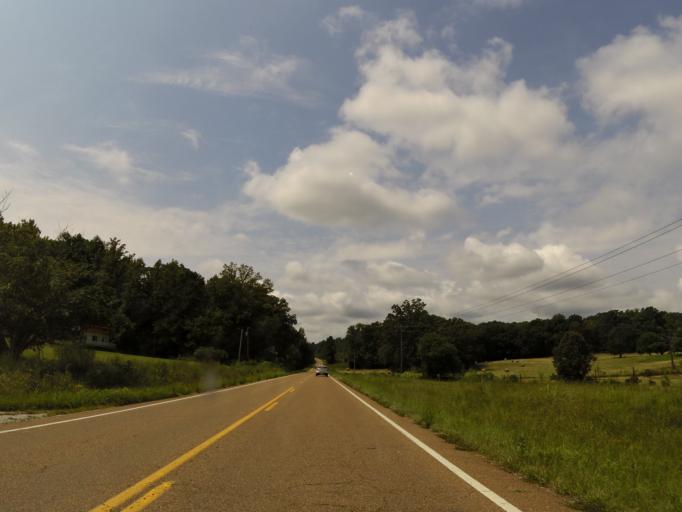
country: US
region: Tennessee
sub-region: Decatur County
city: Decaturville
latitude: 35.5437
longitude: -88.2009
